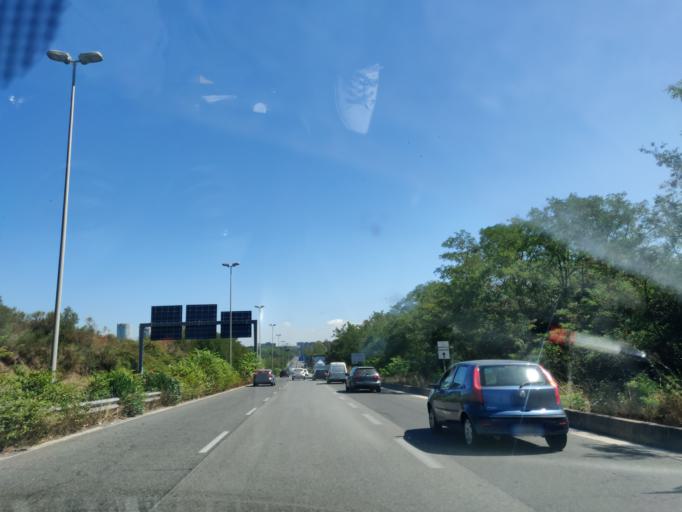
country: IT
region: Latium
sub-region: Citta metropolitana di Roma Capitale
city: Selcetta
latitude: 41.8045
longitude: 12.4549
